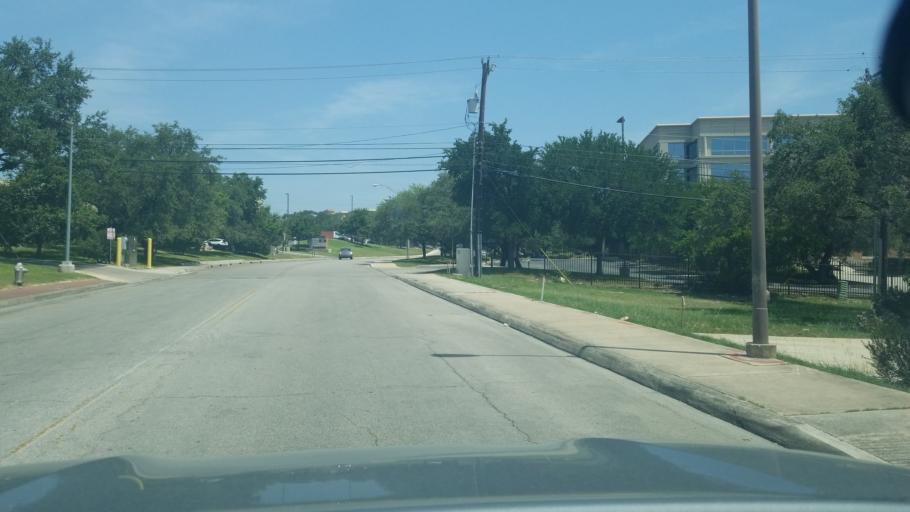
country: US
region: Texas
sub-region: Bexar County
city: Hollywood Park
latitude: 29.6129
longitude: -98.4834
